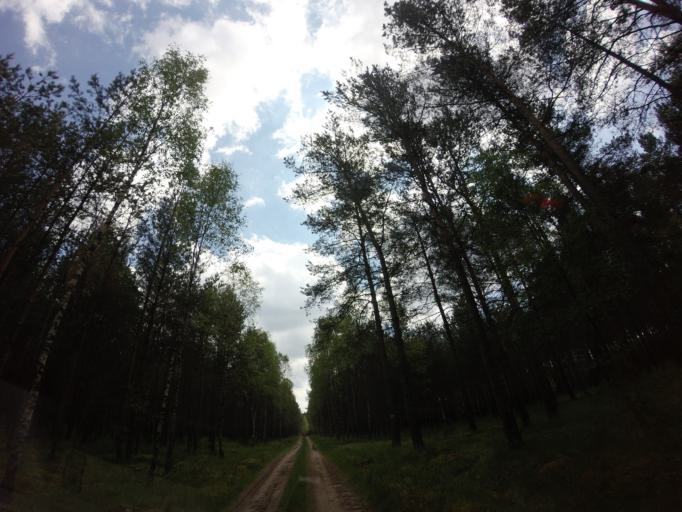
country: PL
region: West Pomeranian Voivodeship
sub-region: Powiat drawski
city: Kalisz Pomorski
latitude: 53.2214
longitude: 15.9396
